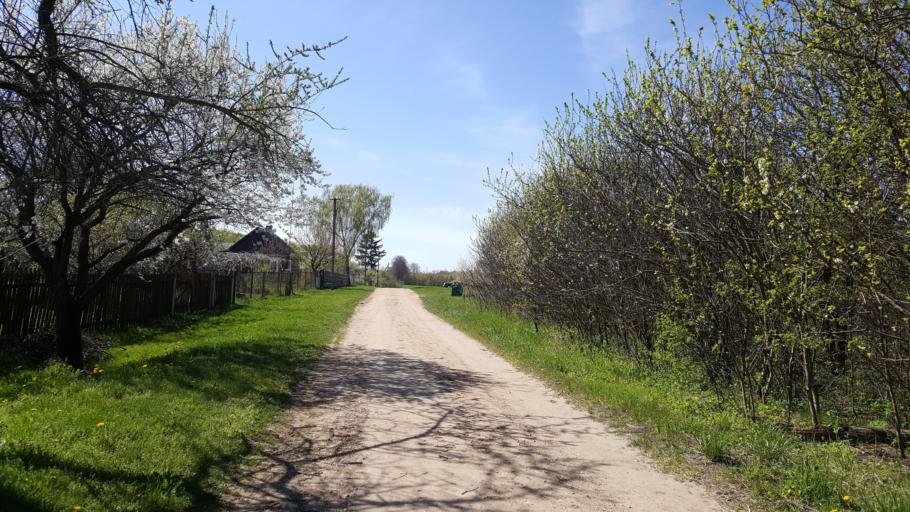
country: BY
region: Brest
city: Vysokaye
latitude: 52.3536
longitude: 23.4388
